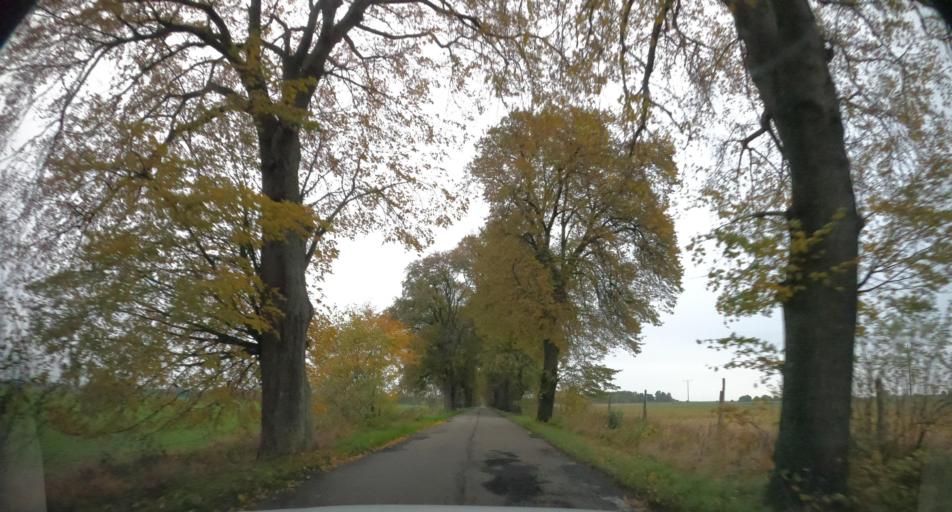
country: PL
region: West Pomeranian Voivodeship
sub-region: Powiat kamienski
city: Wolin
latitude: 53.9011
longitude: 14.6274
